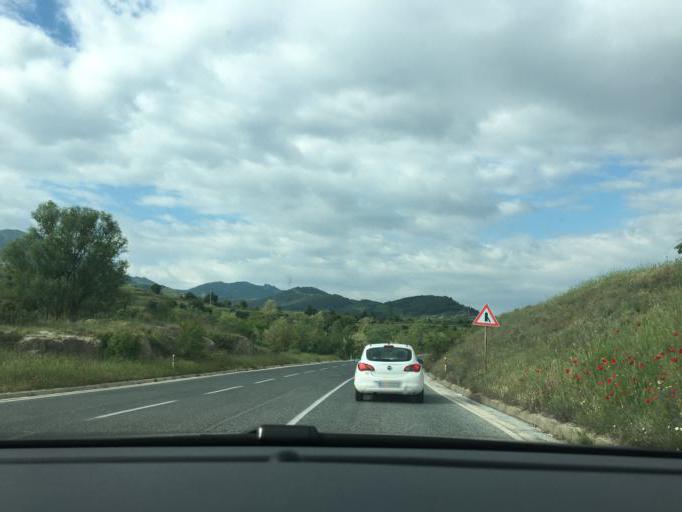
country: MK
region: Prilep
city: Prilep
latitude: 41.3658
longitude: 21.6086
